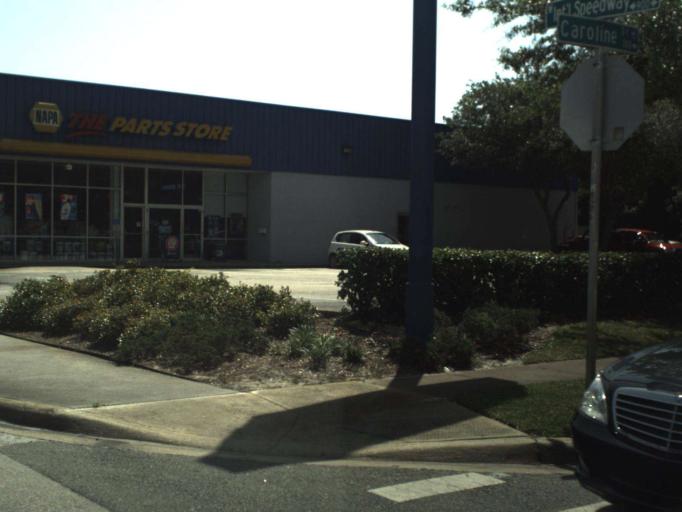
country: US
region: Florida
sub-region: Volusia County
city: Daytona Beach
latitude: 29.2041
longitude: -81.0379
